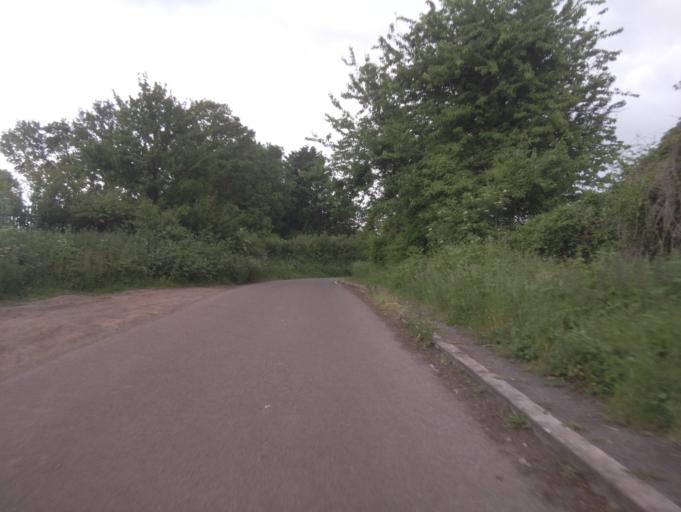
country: GB
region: England
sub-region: South Gloucestershire
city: Pucklechurch
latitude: 51.4621
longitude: -2.4220
